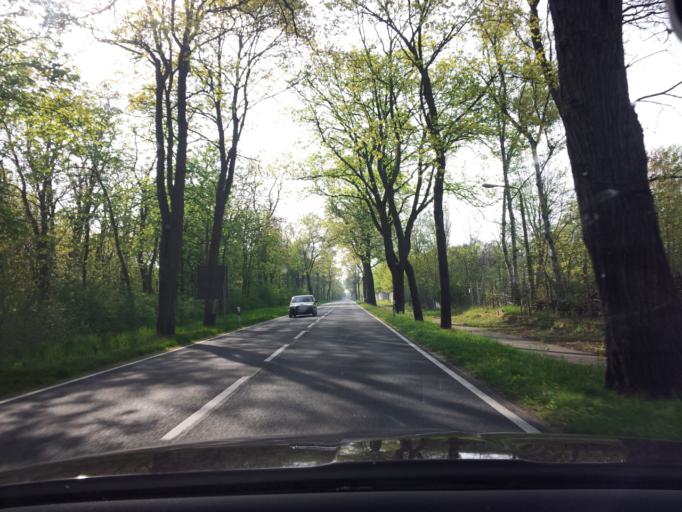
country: DE
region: Brandenburg
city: Niedergorsdorf
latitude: 52.0031
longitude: 13.0233
